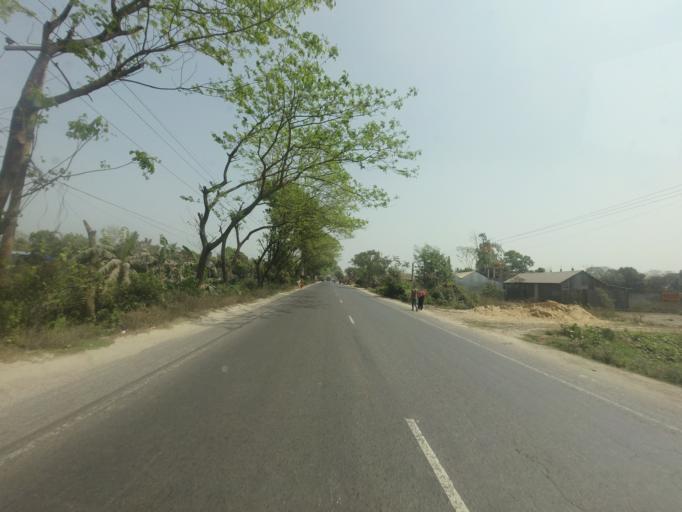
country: BD
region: Dhaka
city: Bhairab Bazar
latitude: 24.0396
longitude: 91.0336
